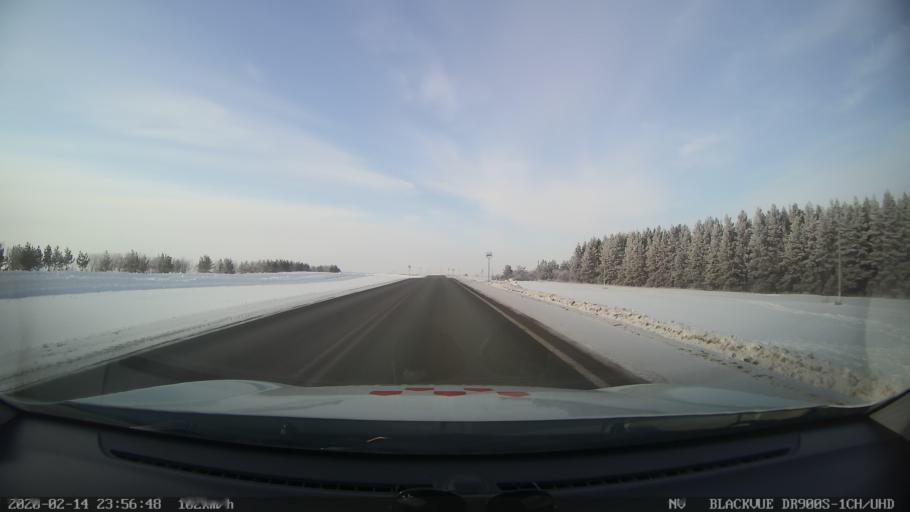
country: RU
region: Tatarstan
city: Kuybyshevskiy Zaton
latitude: 55.3286
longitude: 49.1235
